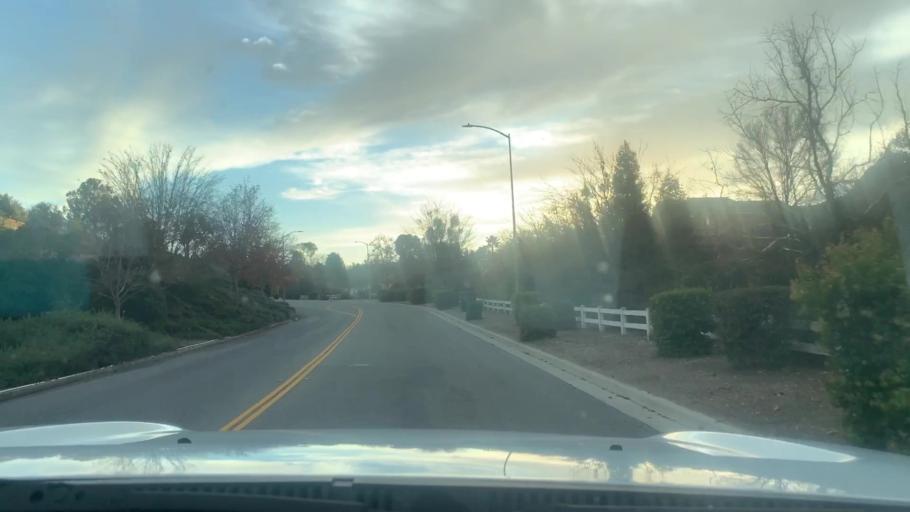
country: US
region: California
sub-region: San Luis Obispo County
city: Paso Robles
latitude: 35.6337
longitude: -120.6587
